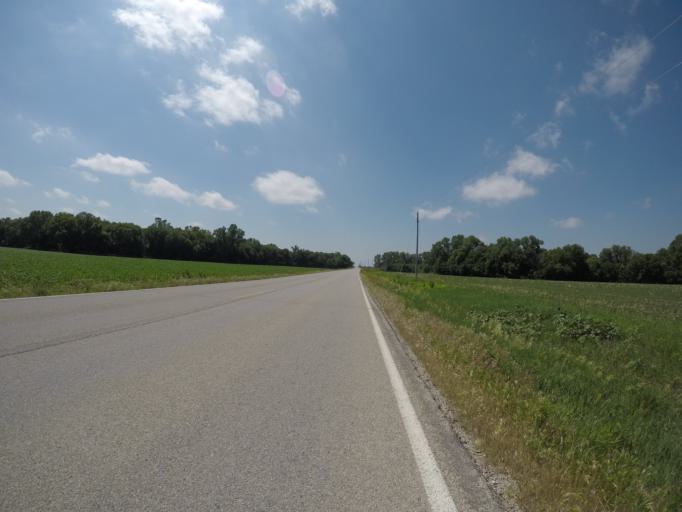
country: US
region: Kansas
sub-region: Pottawatomie County
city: Westmoreland
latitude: 39.3442
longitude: -96.4360
